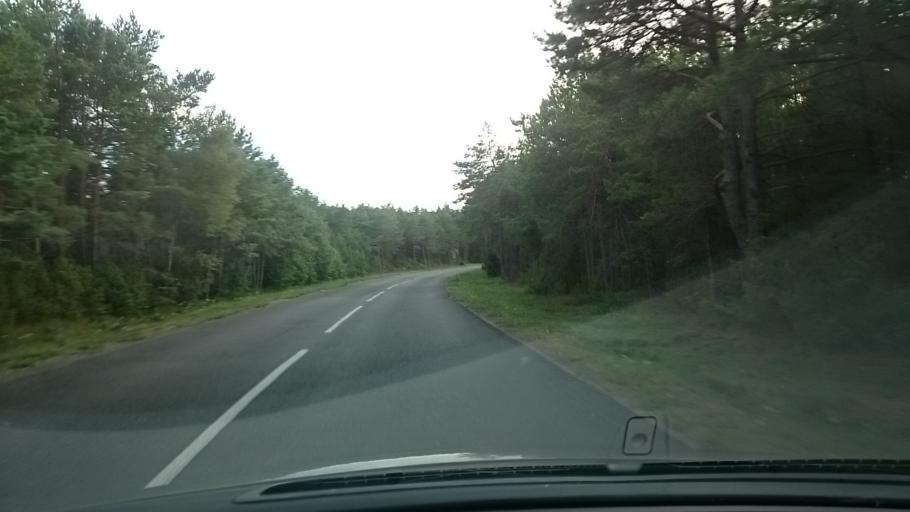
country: EE
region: Saare
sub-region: Kuressaare linn
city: Kuressaare
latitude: 58.4161
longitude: 22.1105
